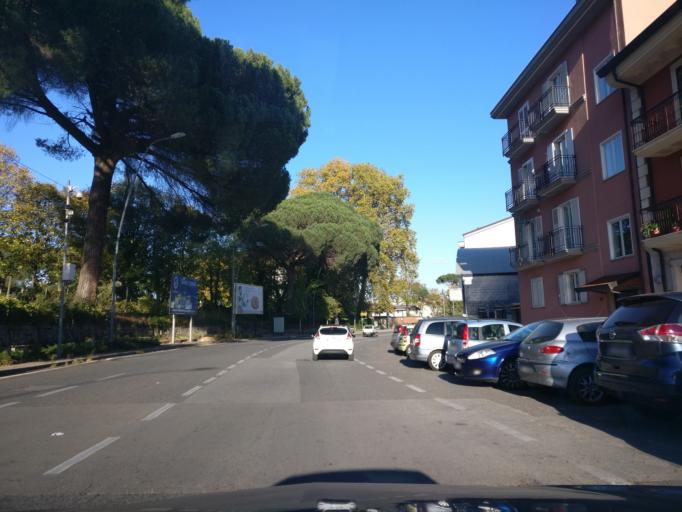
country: IT
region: Campania
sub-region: Provincia di Avellino
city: Torelli-Torrette
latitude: 40.9112
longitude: 14.7706
